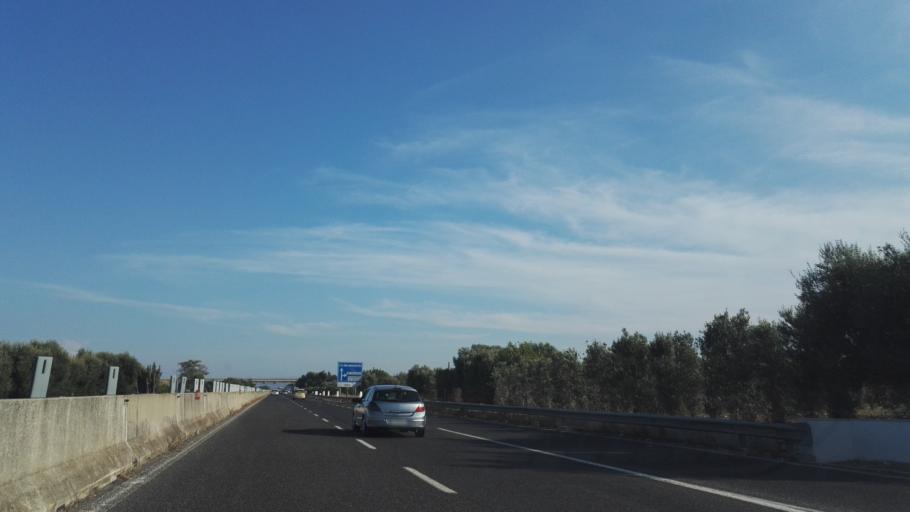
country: IT
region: Apulia
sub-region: Provincia di Bari
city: Monopoli
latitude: 40.9107
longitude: 17.3224
